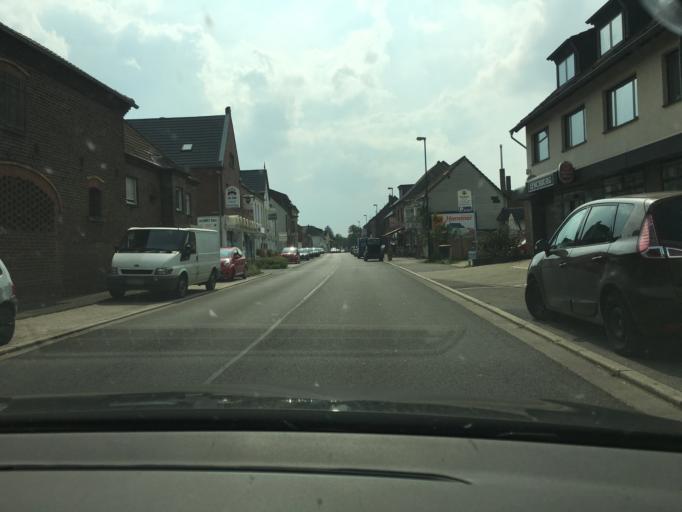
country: DE
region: North Rhine-Westphalia
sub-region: Regierungsbezirk Koln
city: Norvenich
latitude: 50.8544
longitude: 6.6305
